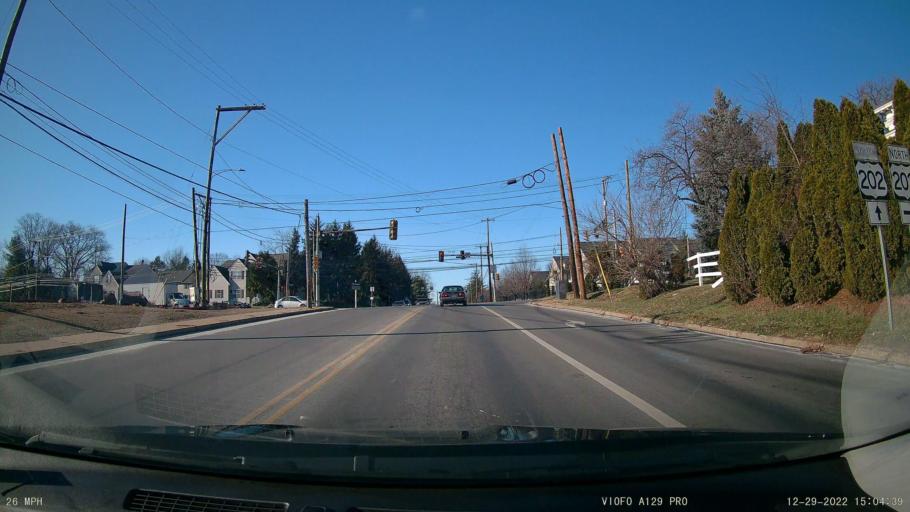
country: US
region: Pennsylvania
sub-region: Montgomery County
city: Norristown
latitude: 40.1293
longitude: -75.3240
